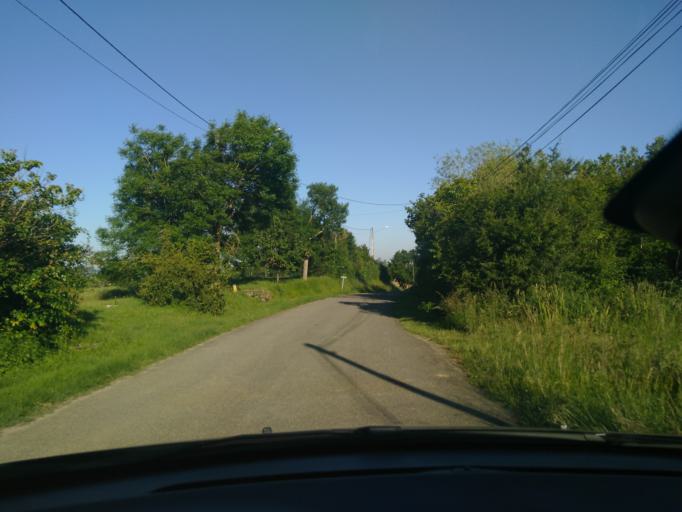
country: FR
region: Midi-Pyrenees
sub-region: Departement du Tarn-et-Garonne
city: Beaumont-de-Lomagne
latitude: 43.7812
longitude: 0.9836
